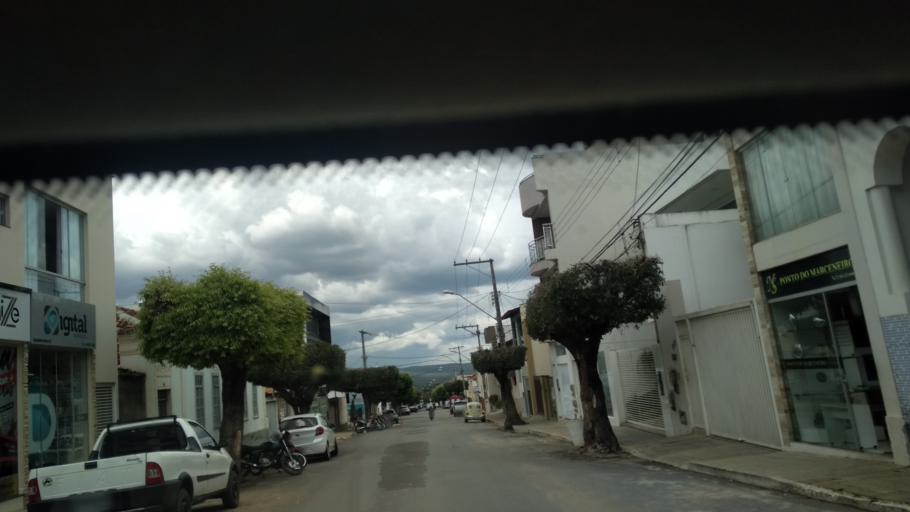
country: BR
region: Bahia
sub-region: Caetite
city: Caetite
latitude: -14.0698
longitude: -42.4886
